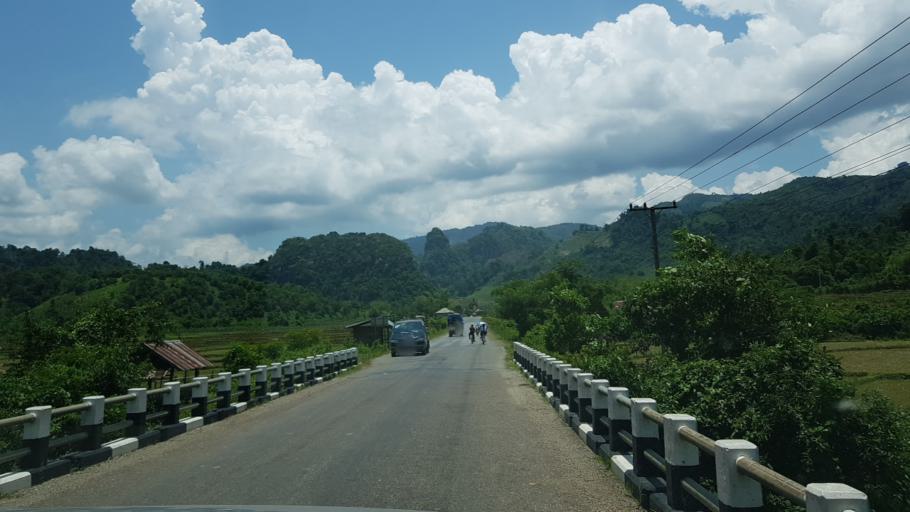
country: LA
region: Vientiane
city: Muang Kasi
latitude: 19.1265
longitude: 102.2454
